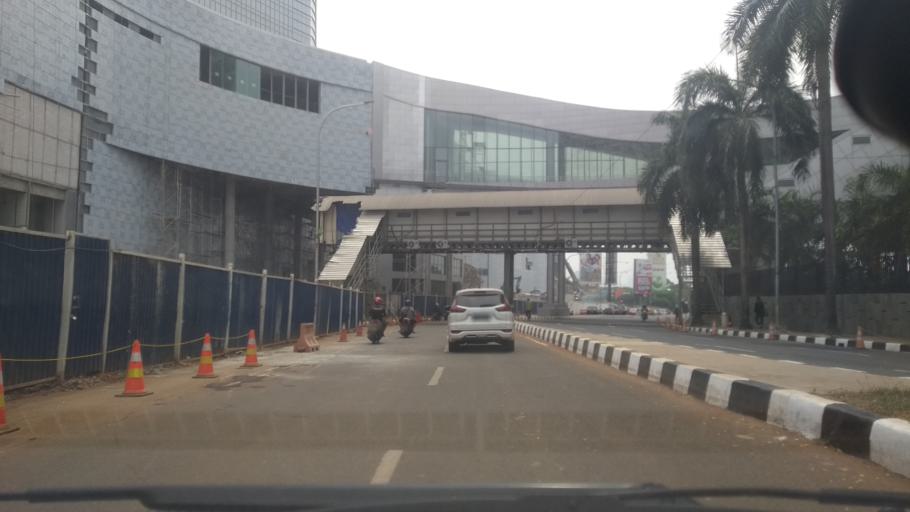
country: ID
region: Banten
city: South Tangerang
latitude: -6.2648
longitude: 106.7819
